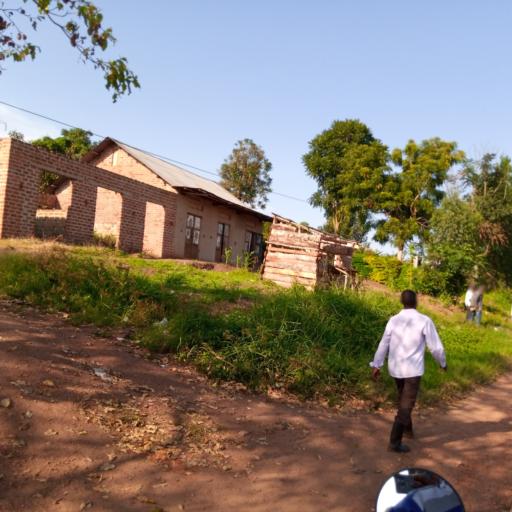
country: UG
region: Central Region
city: Masaka
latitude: -0.4173
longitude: 31.6762
